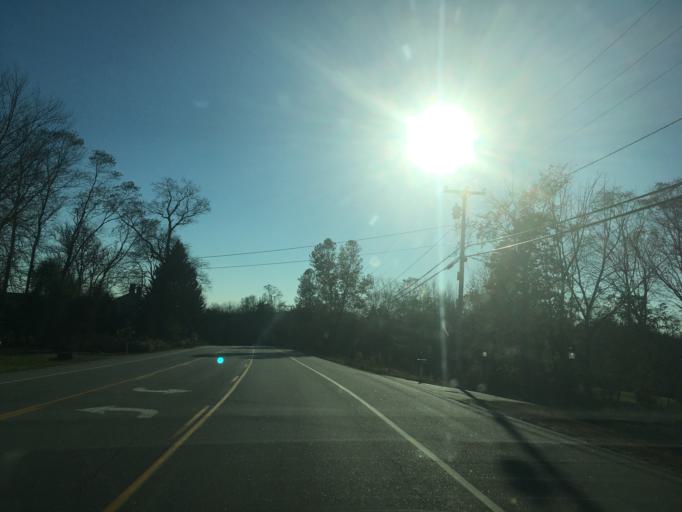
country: US
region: New Hampshire
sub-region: Rockingham County
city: Stratham Station
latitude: 43.0373
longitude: -70.9033
